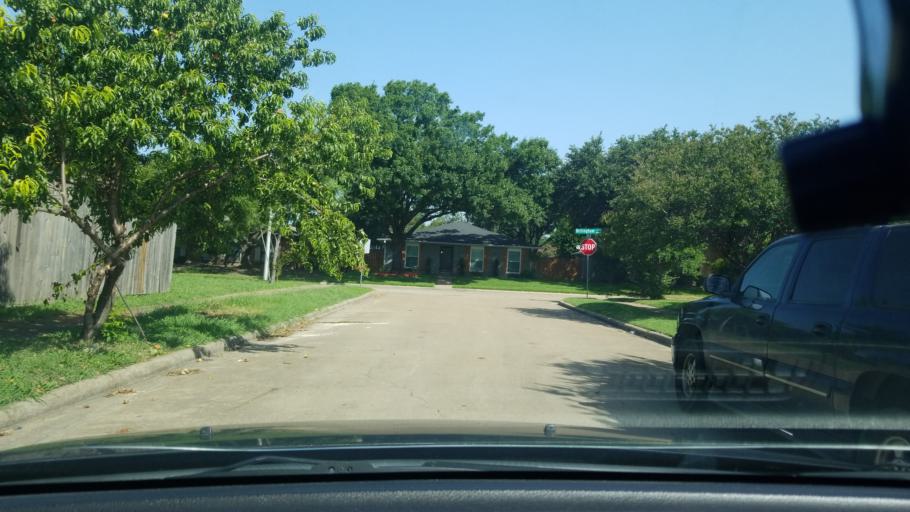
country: US
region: Texas
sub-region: Dallas County
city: Mesquite
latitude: 32.8000
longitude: -96.6924
